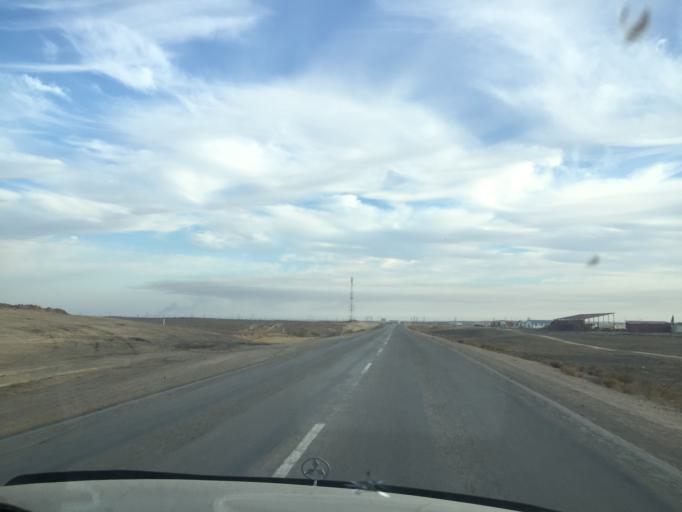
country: KZ
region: Almaty Oblysy
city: Ulken
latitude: 45.1650
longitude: 73.9391
